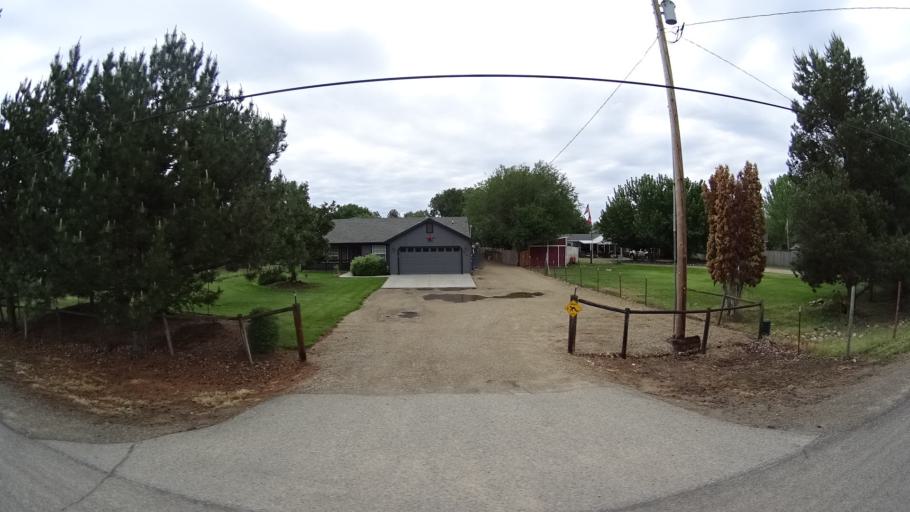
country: US
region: Idaho
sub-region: Ada County
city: Star
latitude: 43.6842
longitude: -116.4932
